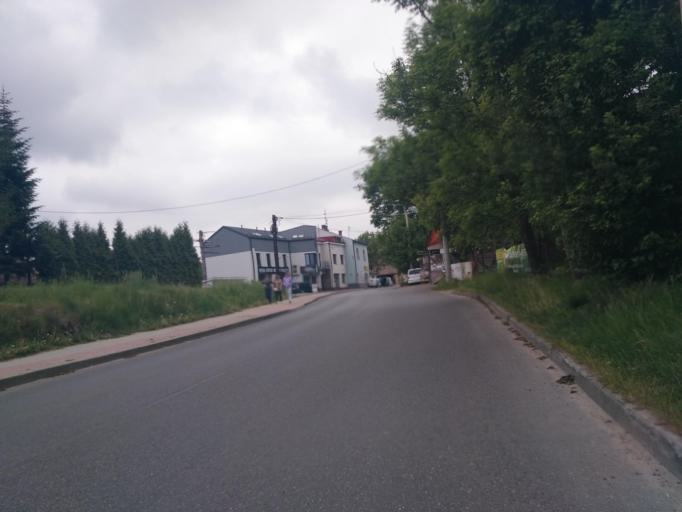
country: PL
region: Subcarpathian Voivodeship
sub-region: Krosno
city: Krosno
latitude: 49.6907
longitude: 21.7622
